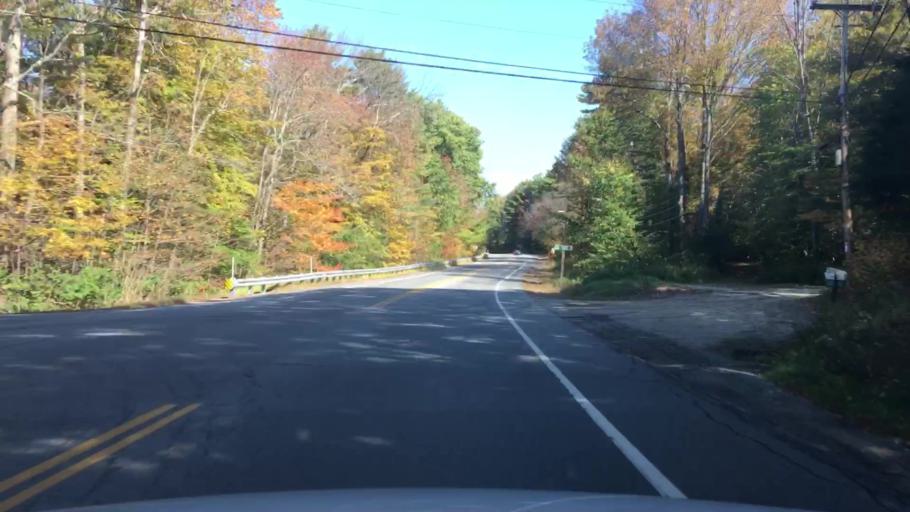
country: US
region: Maine
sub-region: Sagadahoc County
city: Topsham
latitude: 44.0073
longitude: -69.9482
